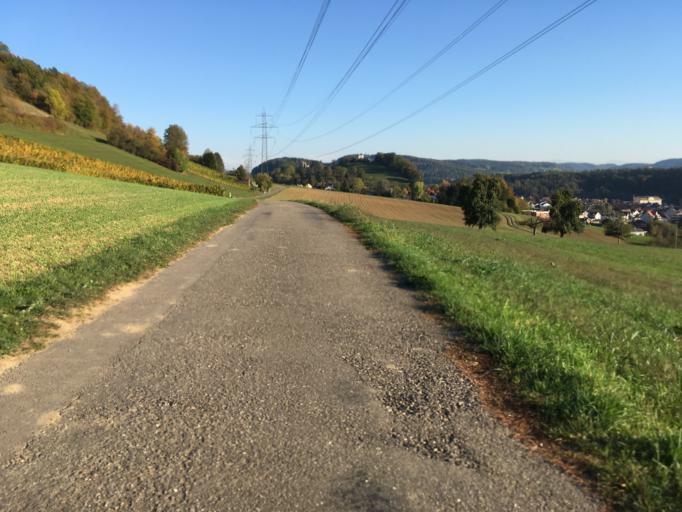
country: CH
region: Zurich
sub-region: Bezirk Buelach
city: Rorbas
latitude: 47.5405
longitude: 8.5769
